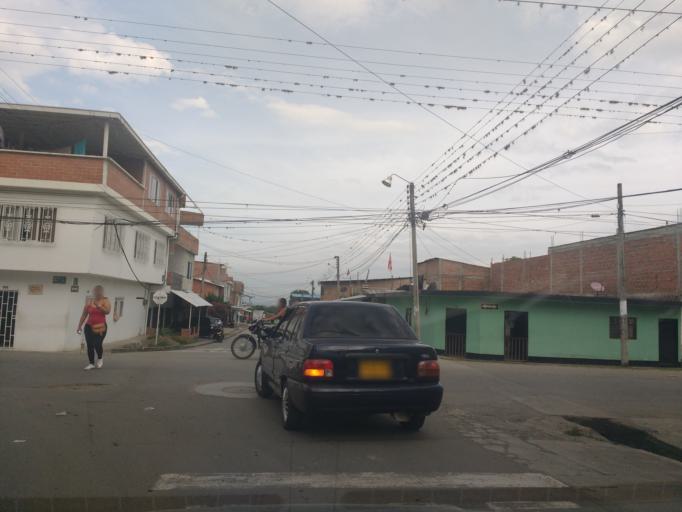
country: CO
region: Cauca
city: Miranda
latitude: 3.2534
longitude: -76.2303
